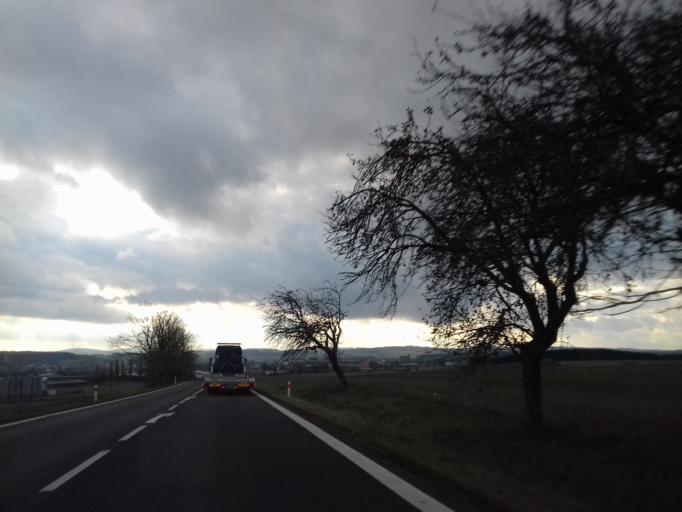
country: CZ
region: Pardubicky
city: Pomezi
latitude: 49.7230
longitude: 16.2982
